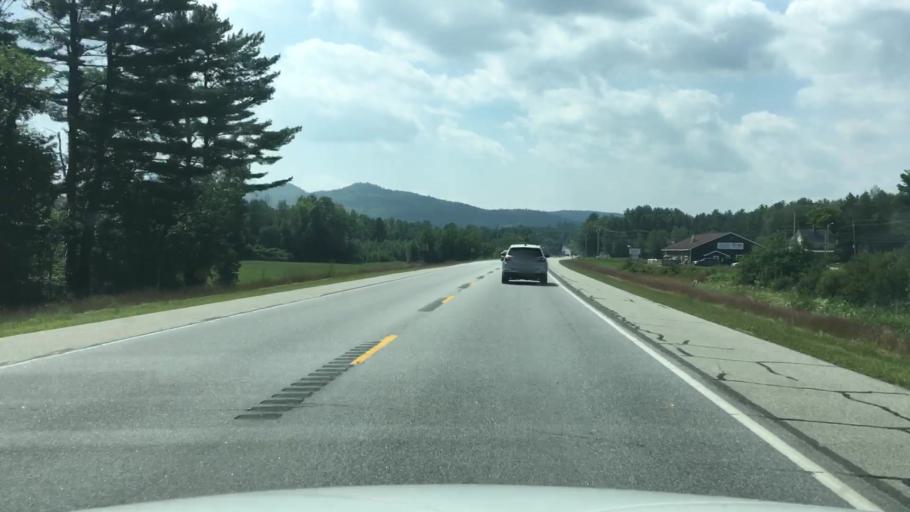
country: US
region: Maine
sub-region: Oxford County
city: Rumford
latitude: 44.5212
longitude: -70.5520
